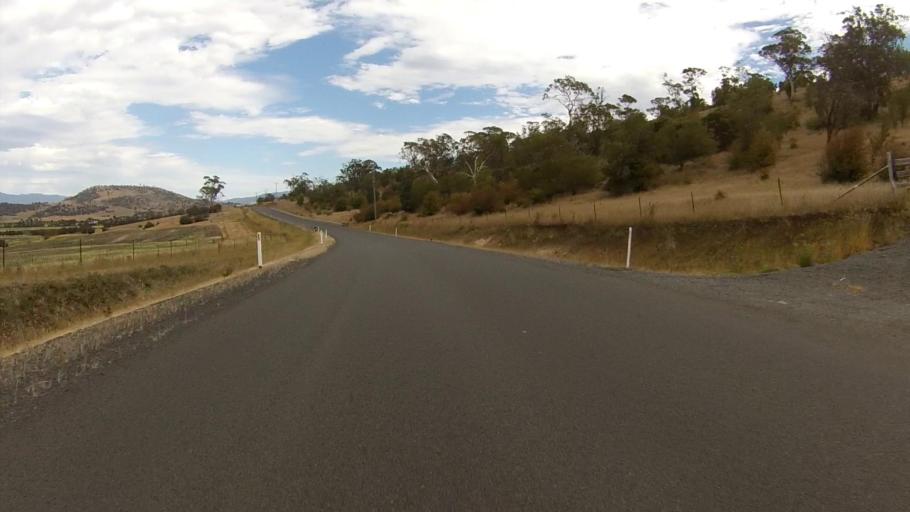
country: AU
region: Tasmania
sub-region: Brighton
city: Old Beach
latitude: -42.7231
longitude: 147.3407
